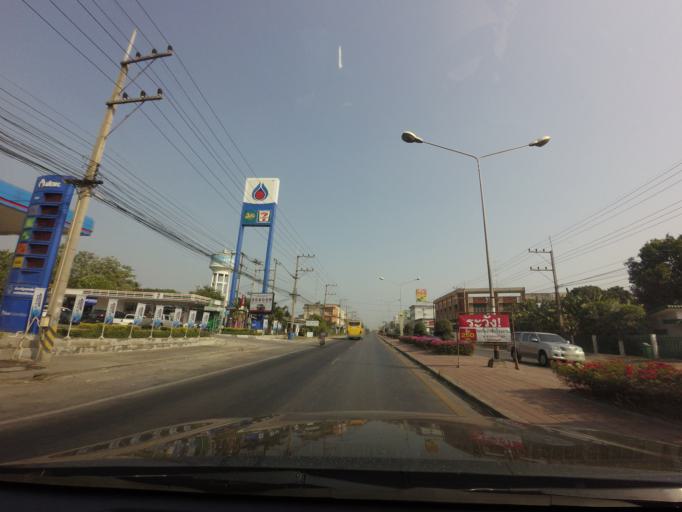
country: TH
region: Kanchanaburi
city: Tha Maka
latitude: 13.8790
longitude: 99.8085
